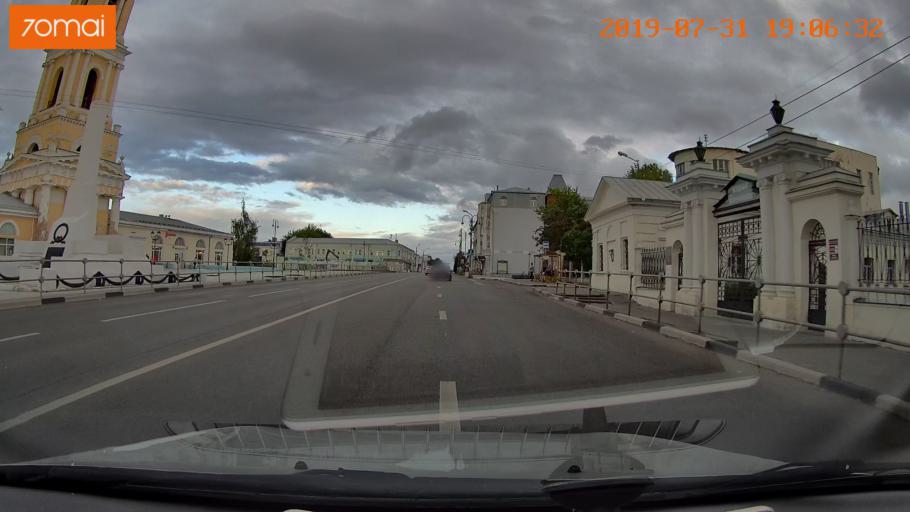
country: RU
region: Moskovskaya
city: Kolomna
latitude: 55.1017
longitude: 38.7543
